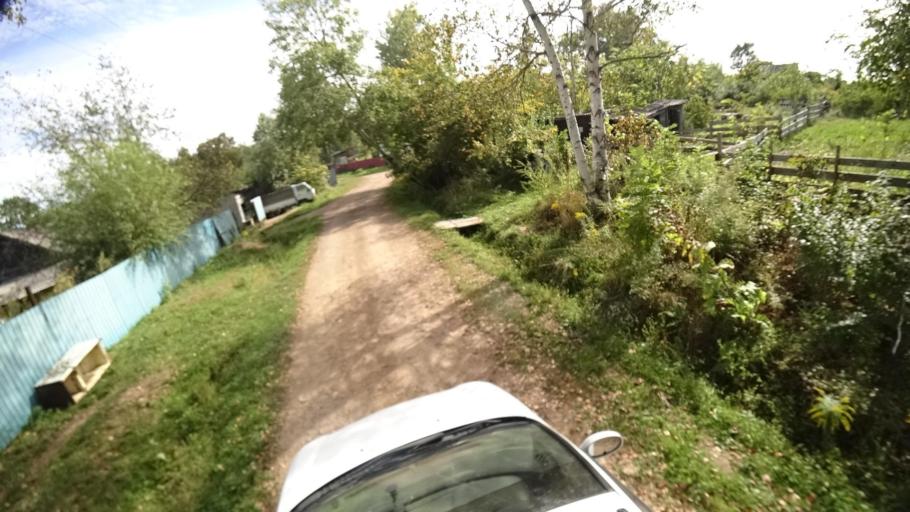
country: RU
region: Primorskiy
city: Yakovlevka
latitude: 44.3889
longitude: 133.6068
